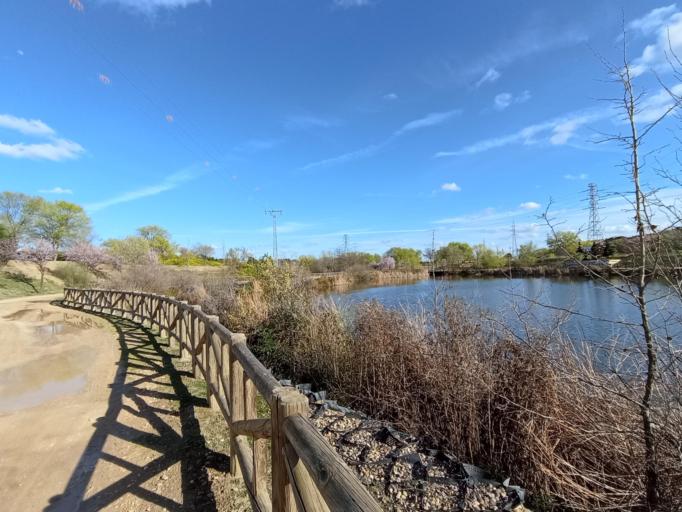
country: ES
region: Madrid
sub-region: Provincia de Madrid
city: Alcorcon
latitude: 40.3583
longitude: -3.8019
